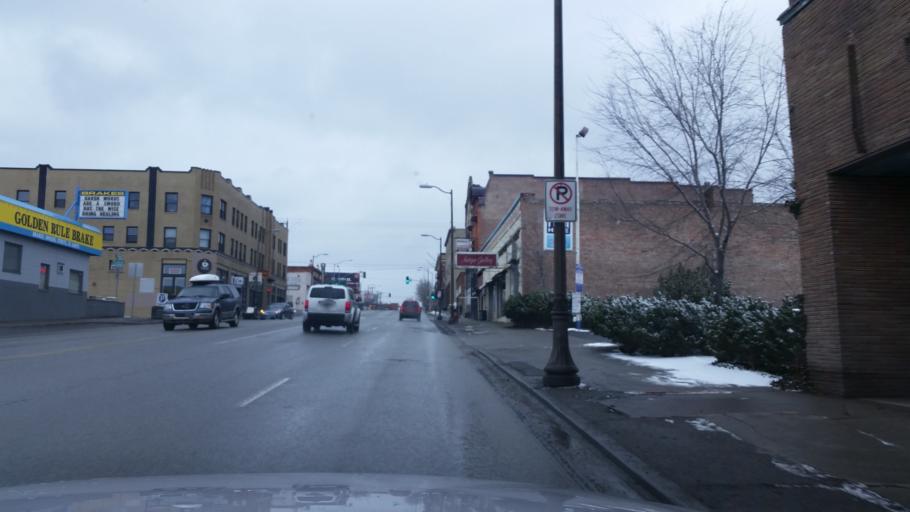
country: US
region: Washington
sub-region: Spokane County
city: Spokane
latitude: 47.6630
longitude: -117.4265
